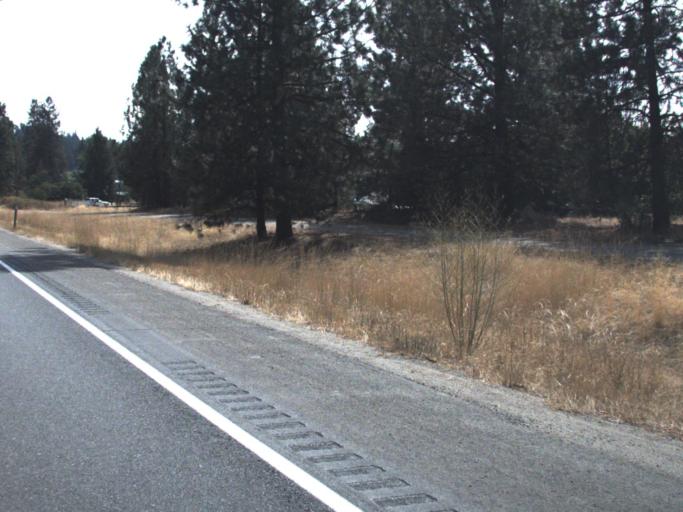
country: US
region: Washington
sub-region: Spokane County
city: Deer Park
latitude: 48.0465
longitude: -117.6088
